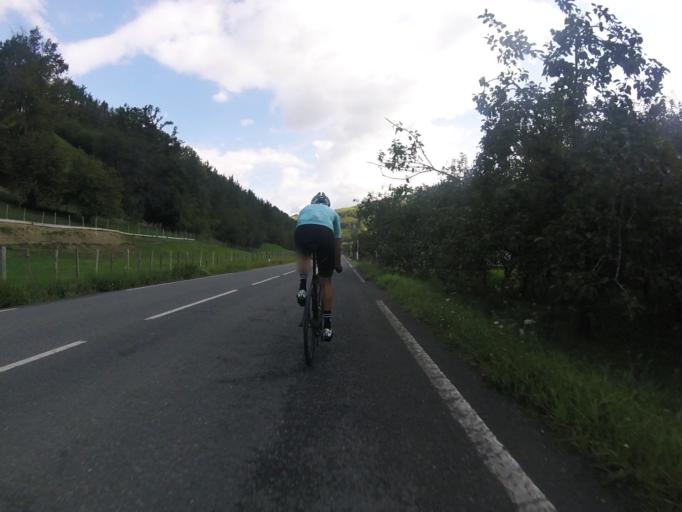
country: ES
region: Basque Country
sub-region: Provincia de Guipuzcoa
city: Amezqueta
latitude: 43.0637
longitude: -2.0869
